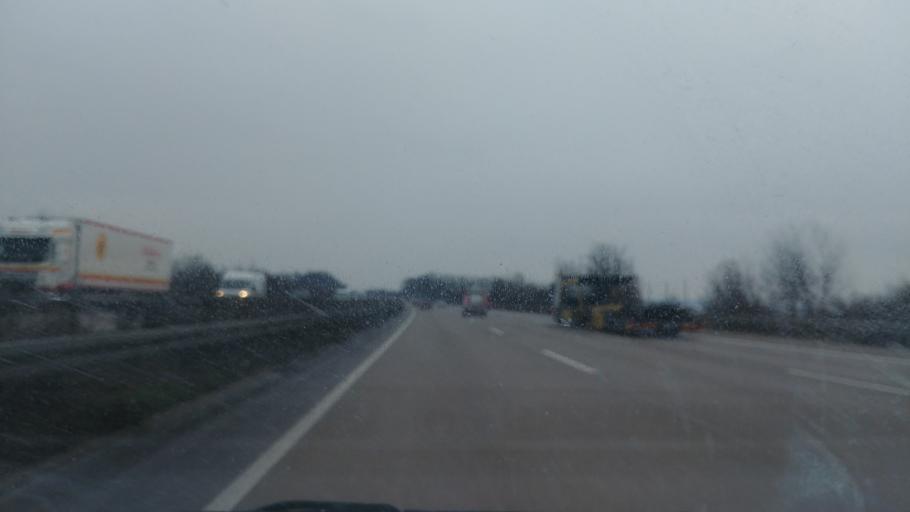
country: DE
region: Lower Saxony
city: Harsum
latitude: 52.1973
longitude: 9.9449
